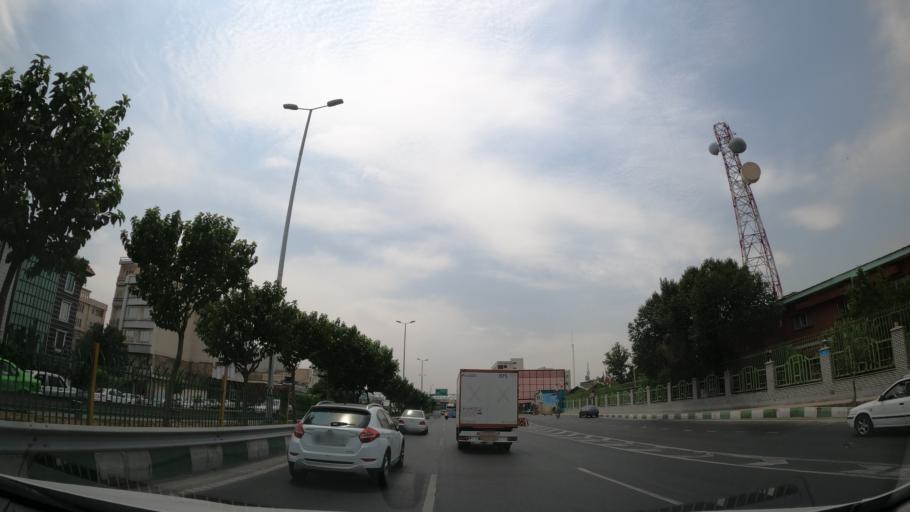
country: IR
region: Tehran
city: Tehran
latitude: 35.6778
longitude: 51.3297
